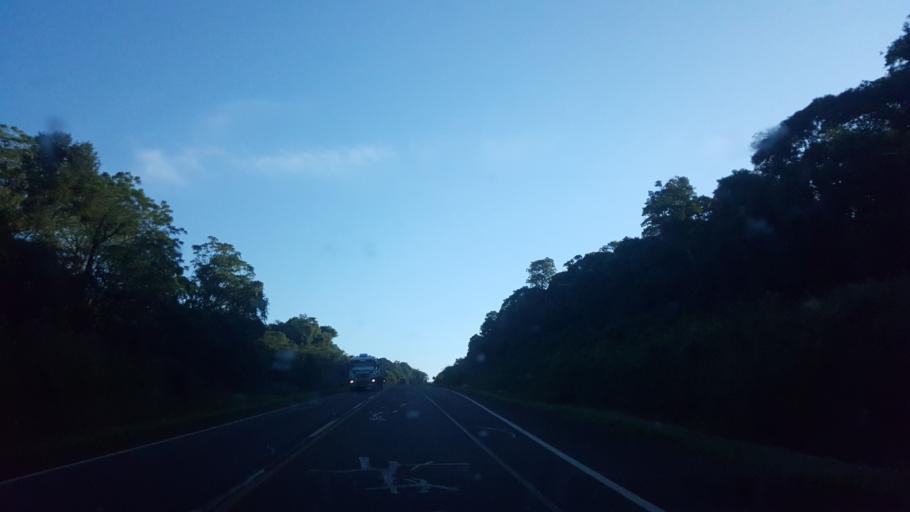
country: AR
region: Misiones
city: El Alcazar
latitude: -26.7094
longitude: -54.8466
